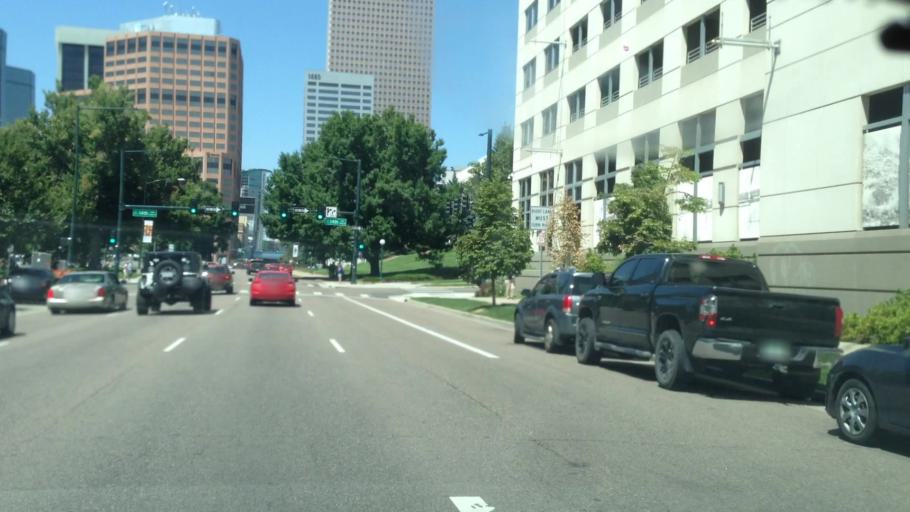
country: US
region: Colorado
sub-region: Denver County
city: Denver
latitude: 39.7378
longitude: -104.9861
